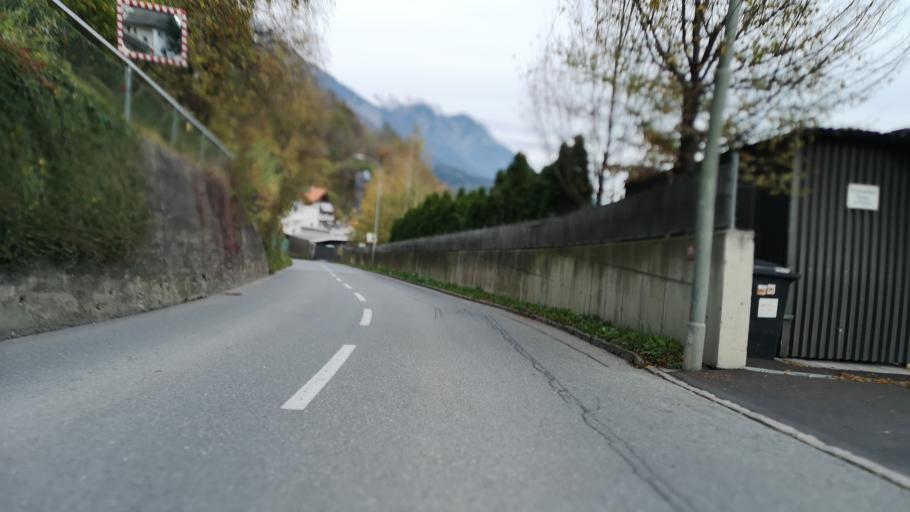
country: AT
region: Tyrol
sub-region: Innsbruck Stadt
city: Innsbruck
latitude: 47.2760
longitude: 11.3885
